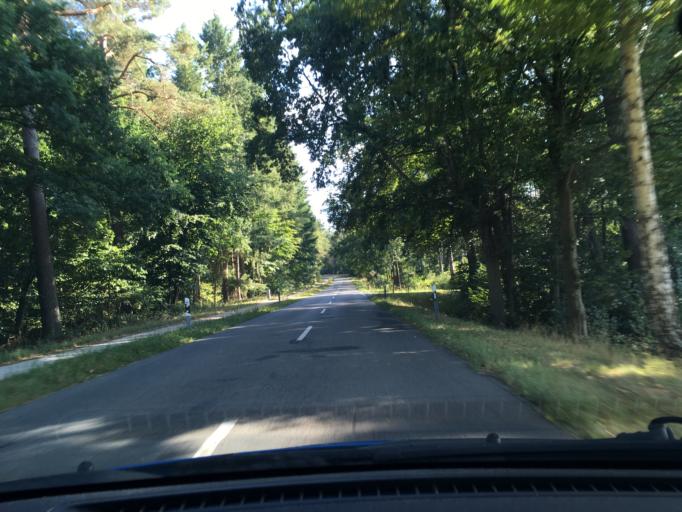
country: DE
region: Lower Saxony
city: Bleckede
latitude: 53.2716
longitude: 10.7174
